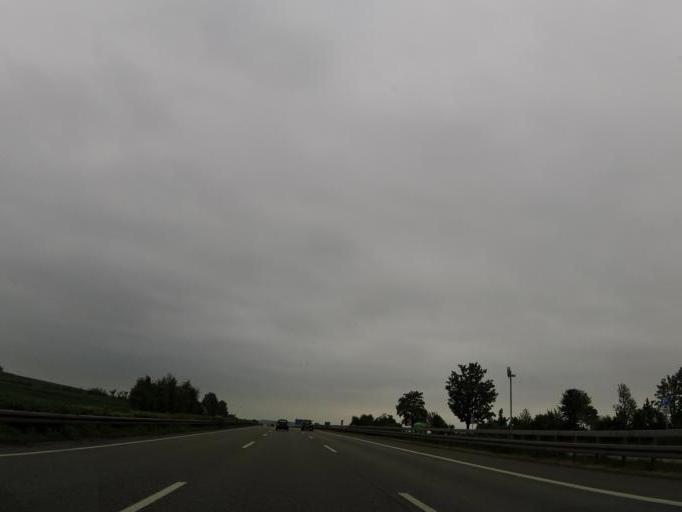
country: DE
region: Lower Saxony
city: Hillerse
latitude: 51.7158
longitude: 9.9414
